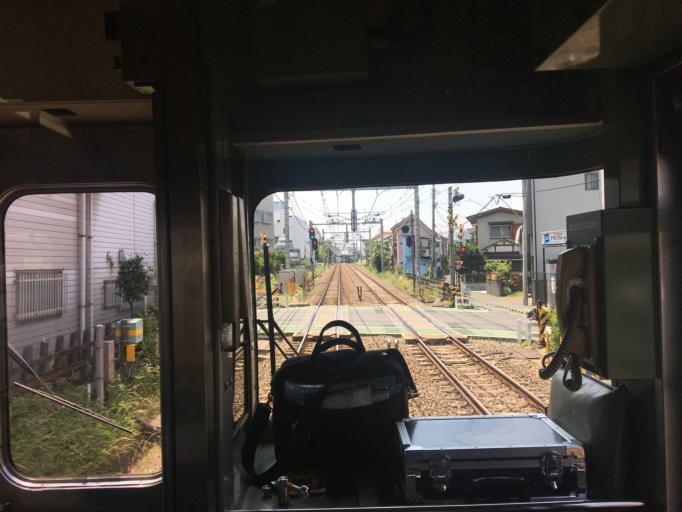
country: JP
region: Tokyo
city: Nishi-Tokyo-shi
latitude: 35.7488
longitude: 139.5732
